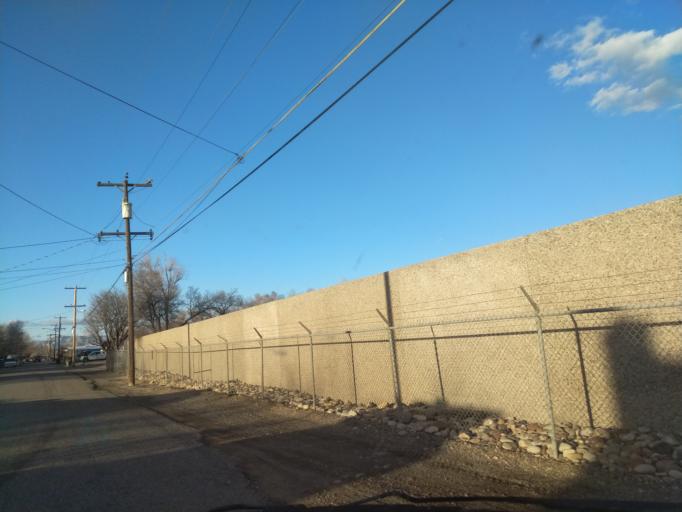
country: US
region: Colorado
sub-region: Mesa County
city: Fruitvale
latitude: 39.0742
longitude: -108.5210
